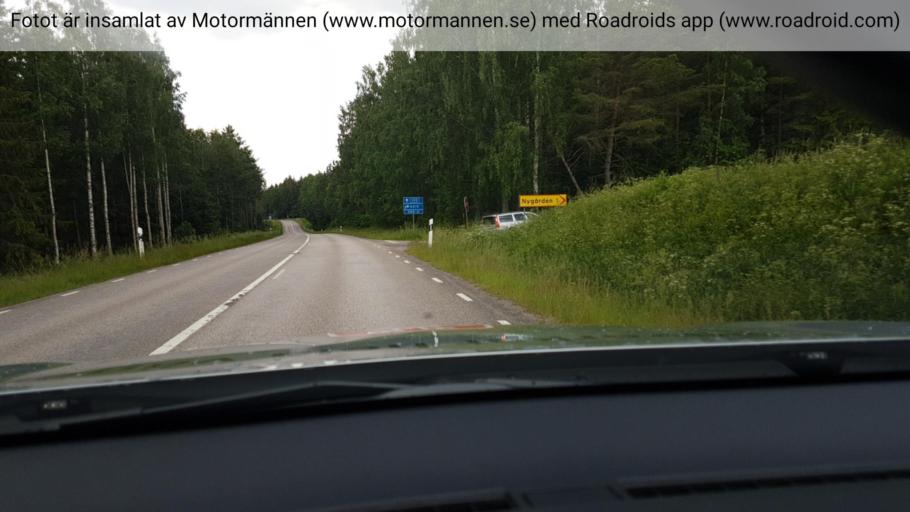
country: SE
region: Vaestra Goetaland
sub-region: Hjo Kommun
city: Hjo
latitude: 58.1873
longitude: 14.2026
